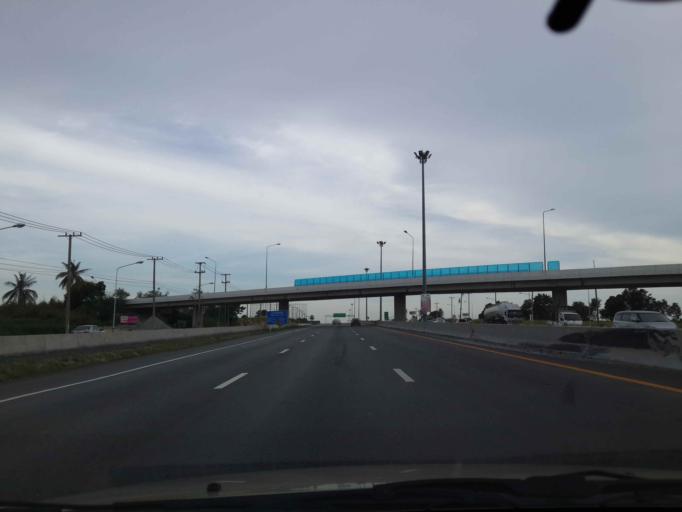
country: TH
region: Chon Buri
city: Ban Talat Bueng
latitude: 12.9948
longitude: 100.9907
